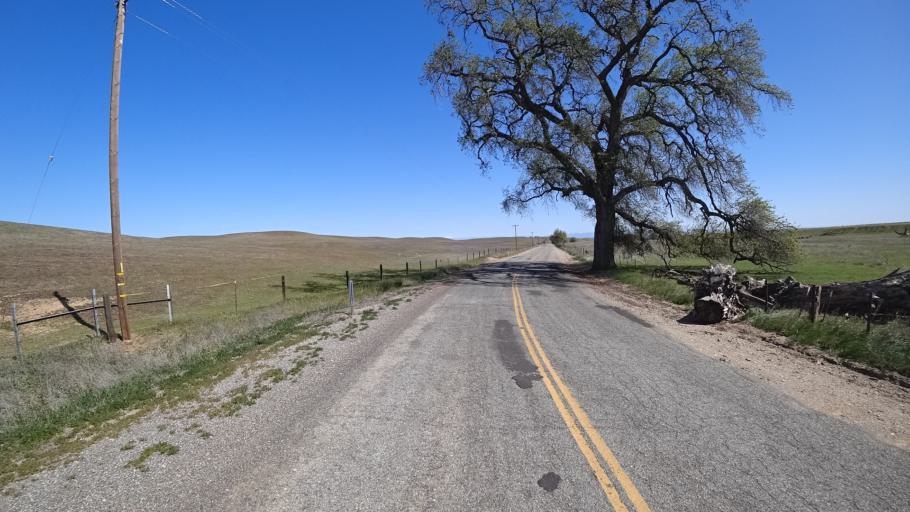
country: US
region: California
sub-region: Glenn County
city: Orland
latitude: 39.7737
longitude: -122.3215
